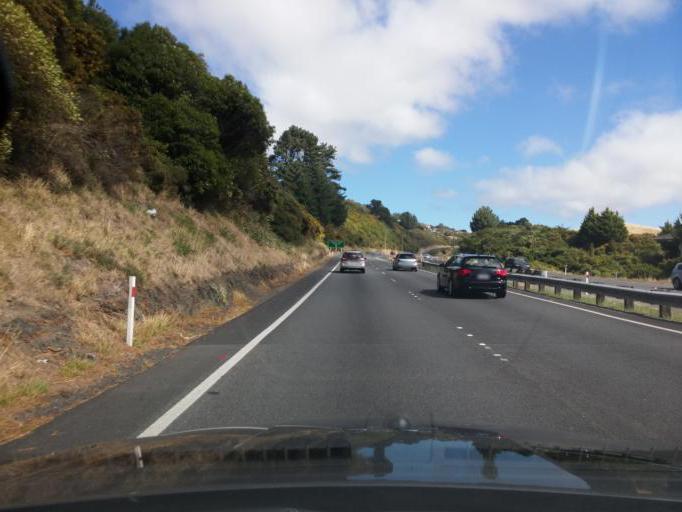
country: NZ
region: Wellington
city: Petone
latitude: -41.1985
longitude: 174.8244
